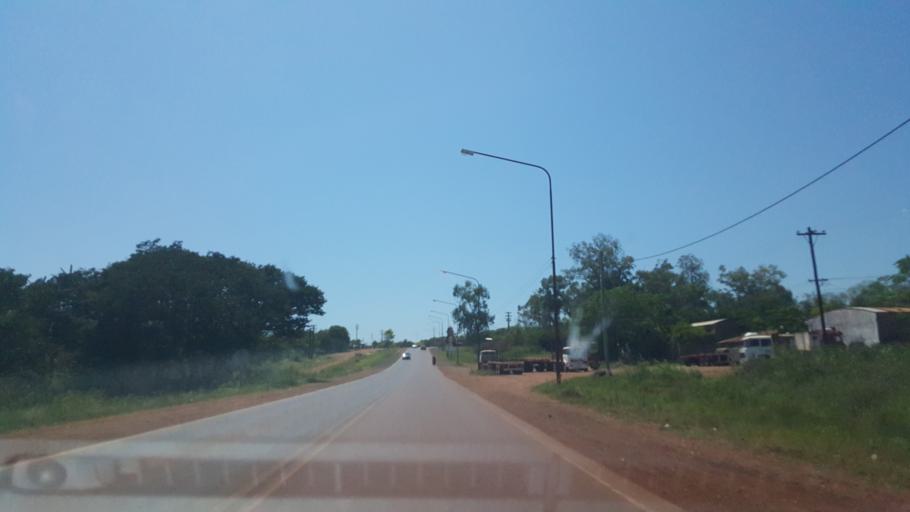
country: AR
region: Corrientes
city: Santo Tome
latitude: -28.5497
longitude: -56.0752
